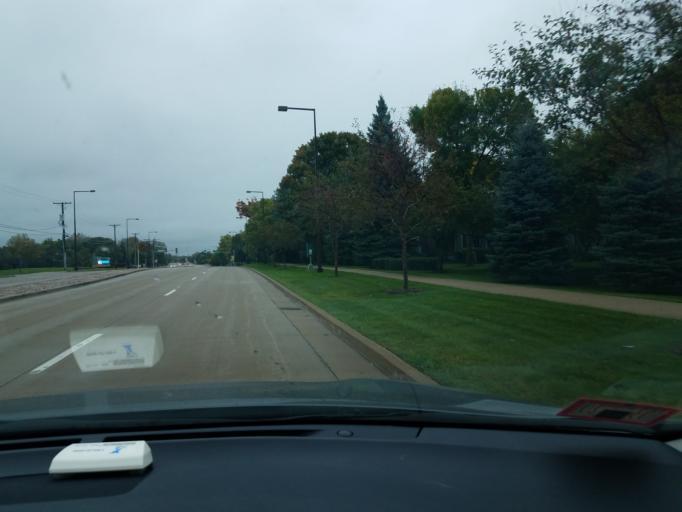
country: US
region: Illinois
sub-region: Lake County
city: Vernon Hills
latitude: 42.1959
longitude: -87.9484
